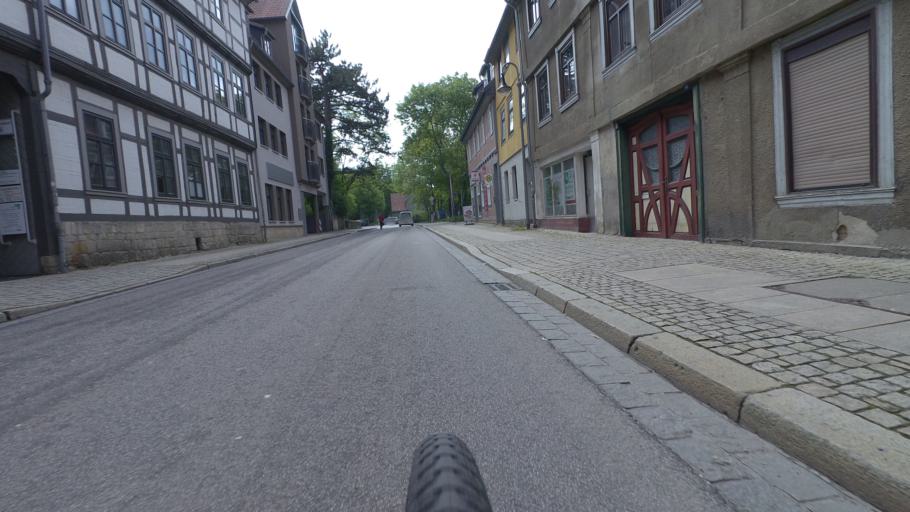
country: DE
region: Saxony-Anhalt
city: Halberstadt
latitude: 51.8945
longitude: 11.0413
